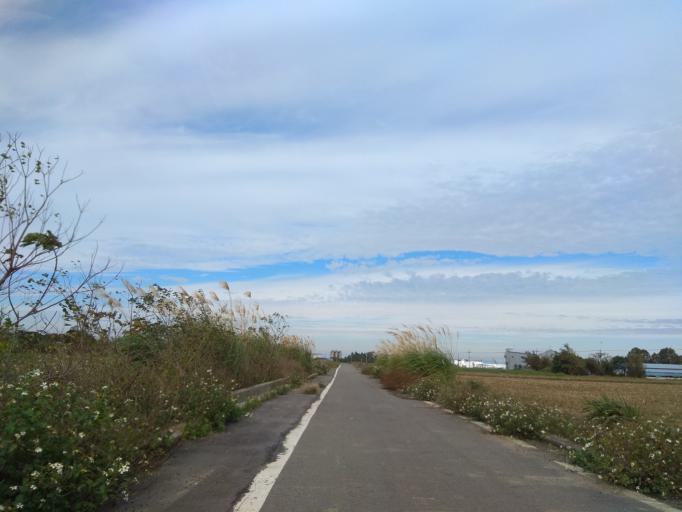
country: TW
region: Taiwan
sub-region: Hsinchu
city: Zhubei
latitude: 24.9576
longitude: 121.1055
